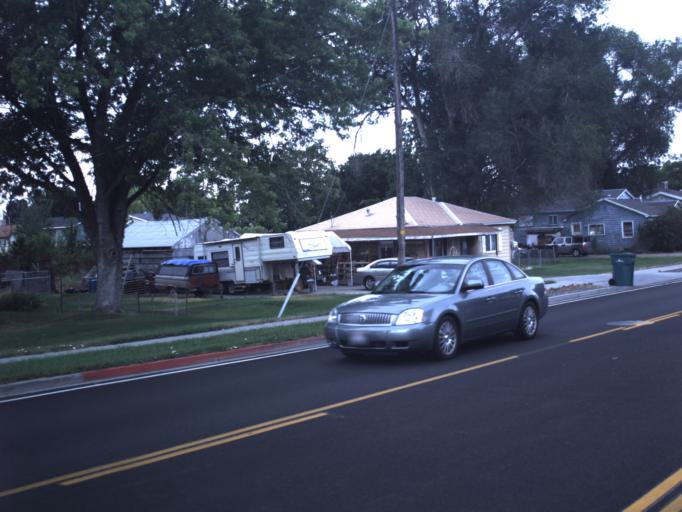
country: US
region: Utah
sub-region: Davis County
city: Clinton
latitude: 41.1617
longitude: -112.0529
